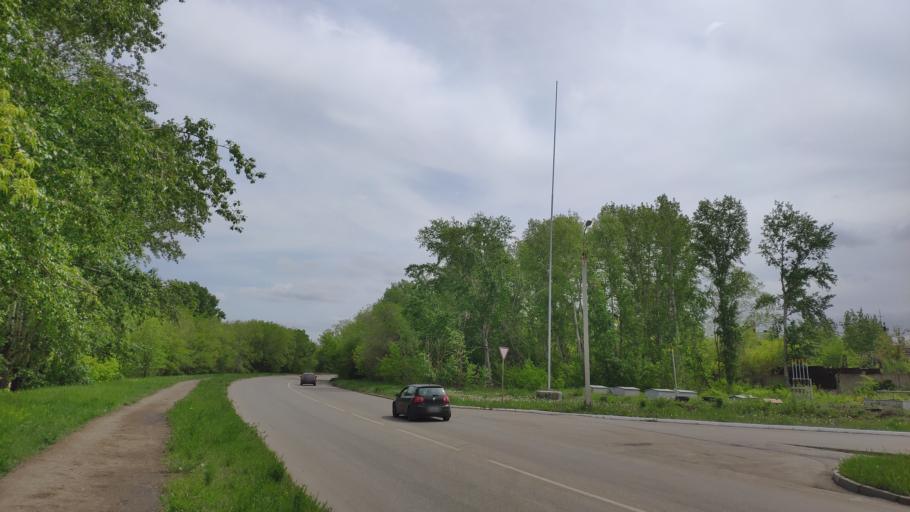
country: RU
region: Chelyabinsk
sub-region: Gorod Magnitogorsk
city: Magnitogorsk
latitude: 53.4167
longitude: 58.9547
